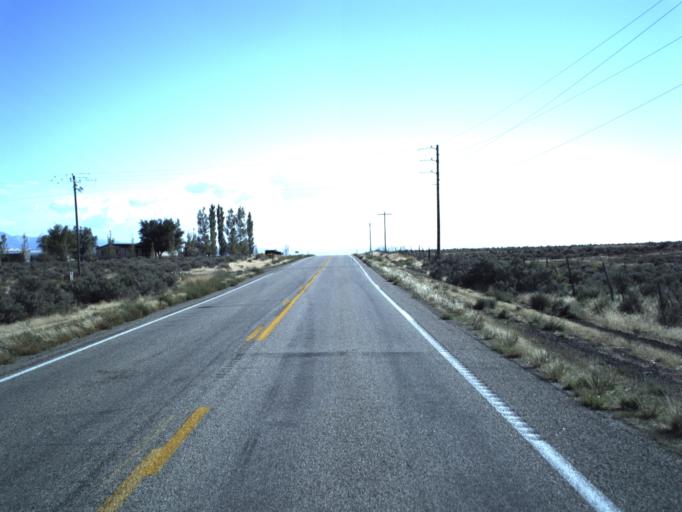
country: US
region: Utah
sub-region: Millard County
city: Fillmore
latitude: 39.1781
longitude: -112.4101
